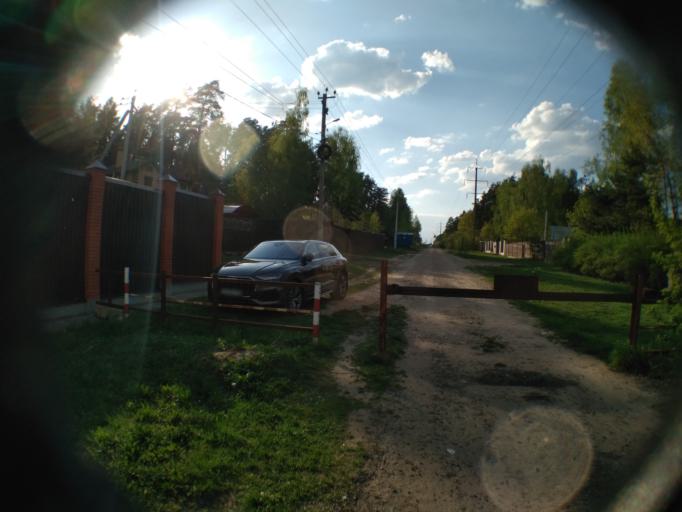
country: RU
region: Moskovskaya
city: Kratovo
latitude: 55.5778
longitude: 38.1708
